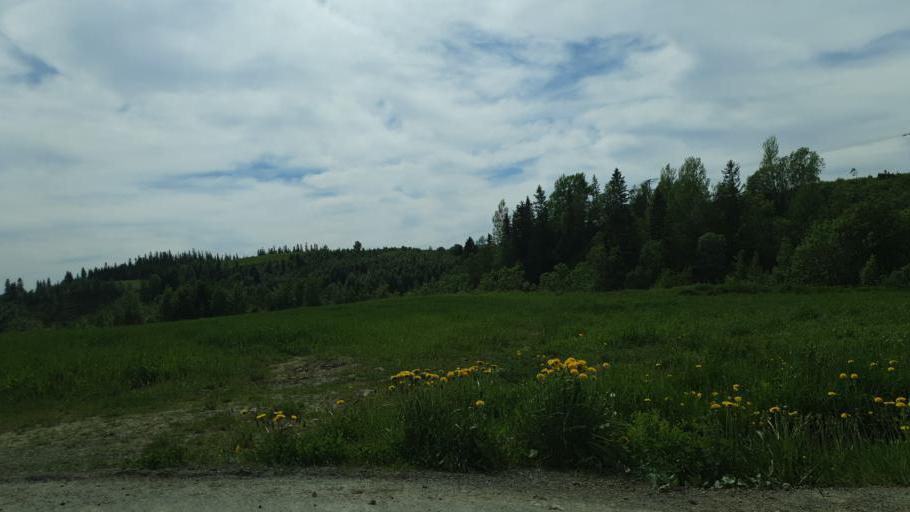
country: NO
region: Nord-Trondelag
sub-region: Leksvik
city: Leksvik
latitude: 63.6858
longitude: 10.5587
